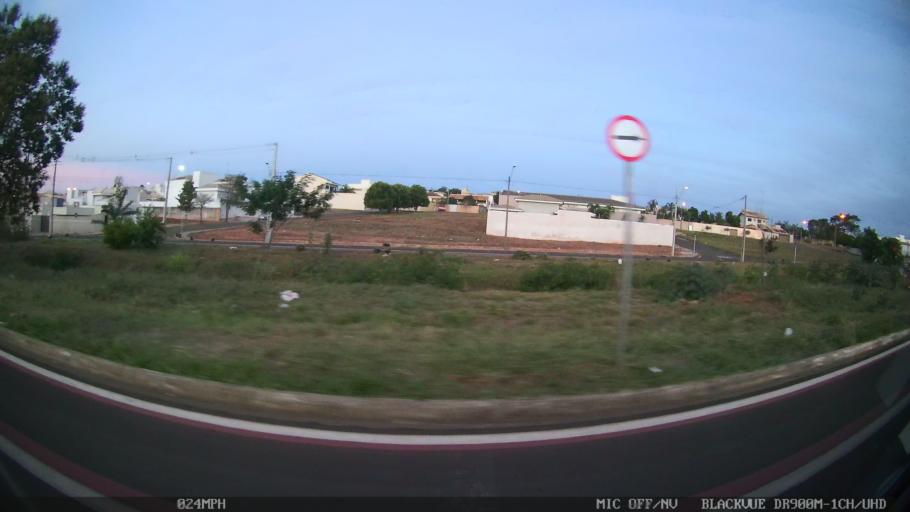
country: BR
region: Sao Paulo
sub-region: Catanduva
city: Catanduva
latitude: -21.1482
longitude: -48.9927
